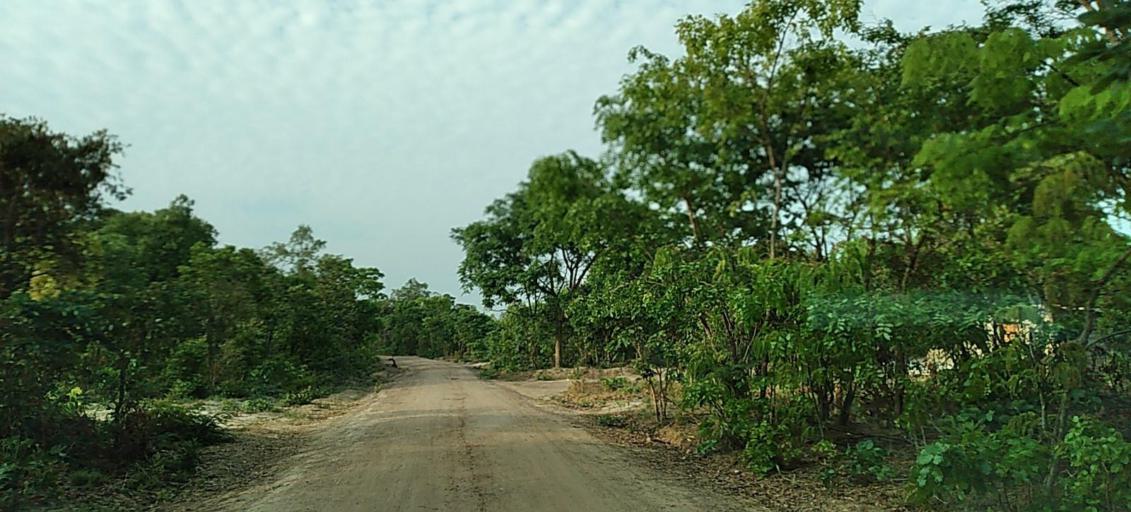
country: ZM
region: Copperbelt
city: Chingola
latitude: -12.8827
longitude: 27.6917
